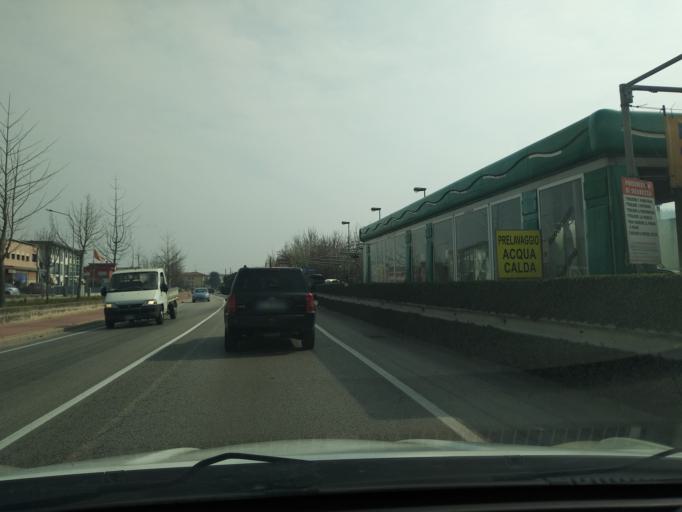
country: IT
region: Veneto
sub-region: Provincia di Vicenza
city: Arzignano
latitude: 45.5272
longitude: 11.3177
